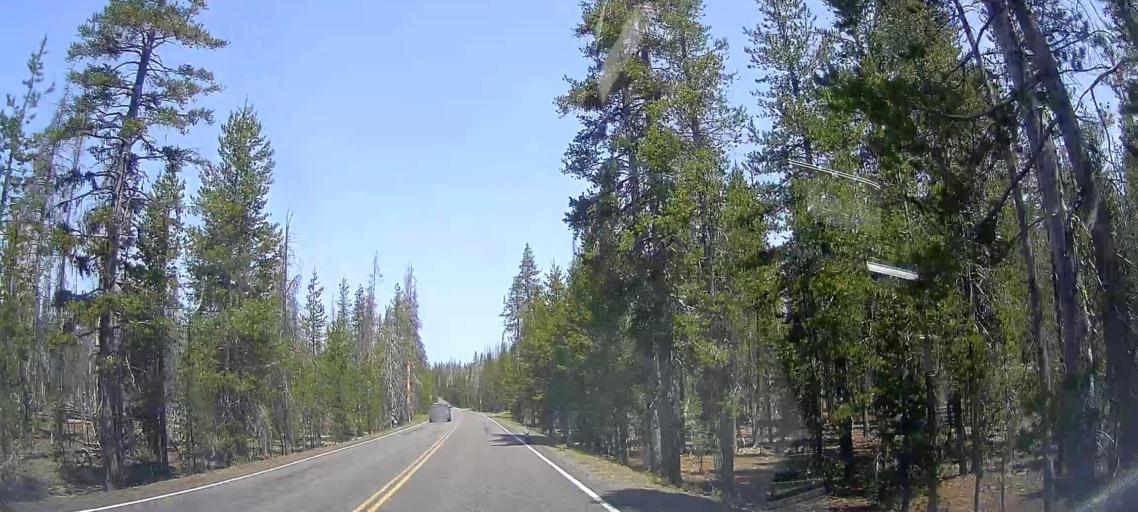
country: US
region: Oregon
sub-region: Lane County
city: Oakridge
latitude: 43.0445
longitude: -122.1183
